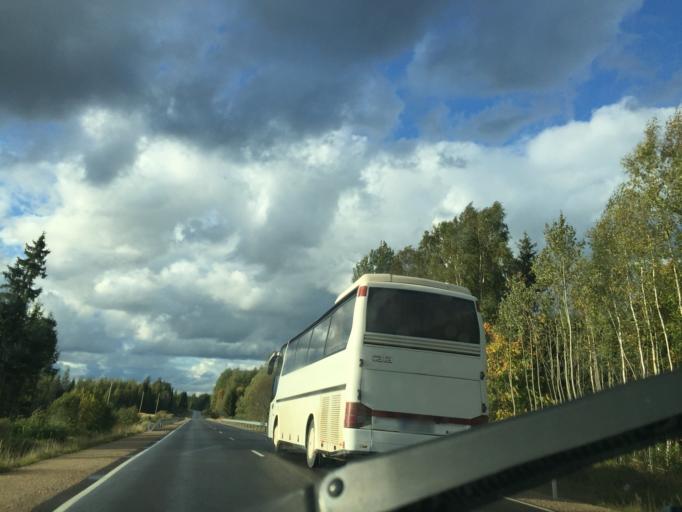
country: LV
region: Ligatne
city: Ligatne
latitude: 57.1456
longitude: 25.0772
